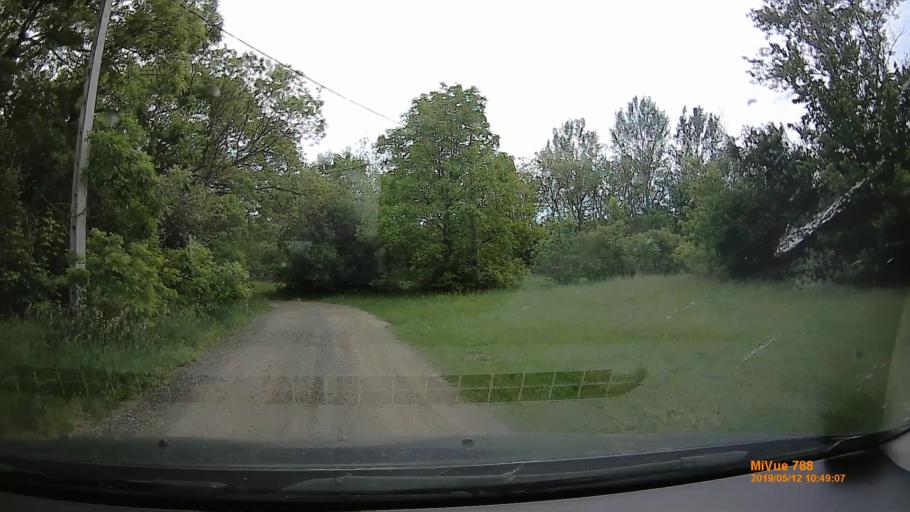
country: HU
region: Budapest
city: Budapest XVII. keruelet
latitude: 47.4797
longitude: 19.2127
